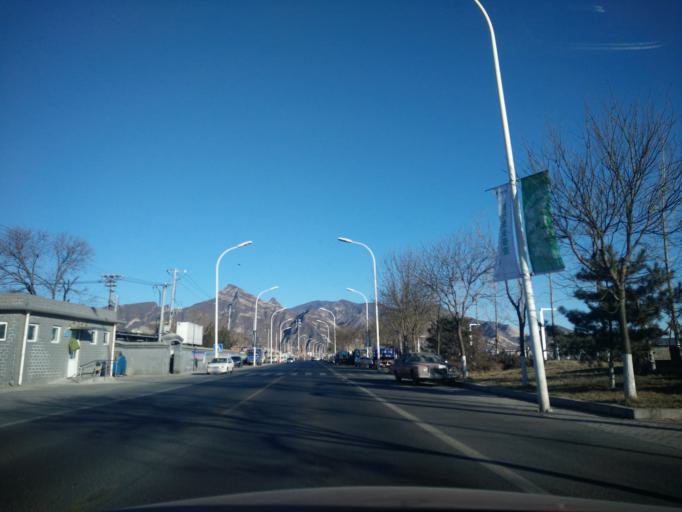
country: CN
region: Beijing
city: Junzhuang
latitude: 39.9804
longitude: 116.0827
